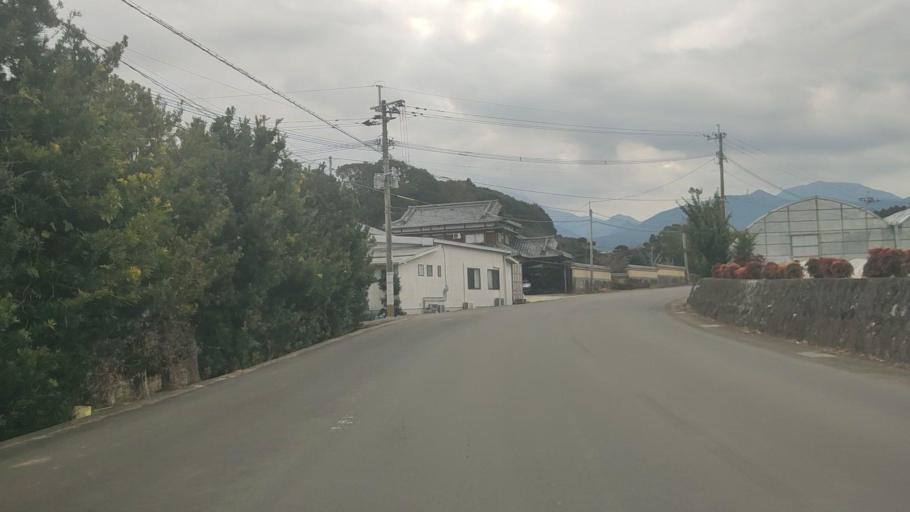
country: JP
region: Nagasaki
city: Shimabara
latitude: 32.8386
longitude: 130.2953
